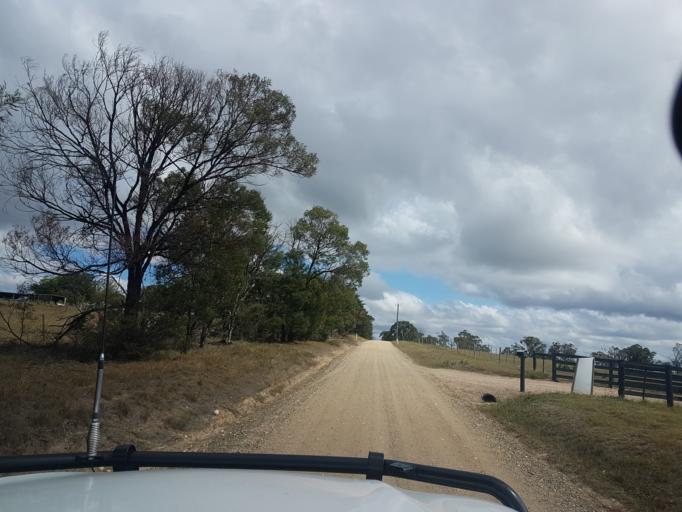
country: AU
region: Victoria
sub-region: East Gippsland
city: Bairnsdale
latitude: -37.7837
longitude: 147.5274
